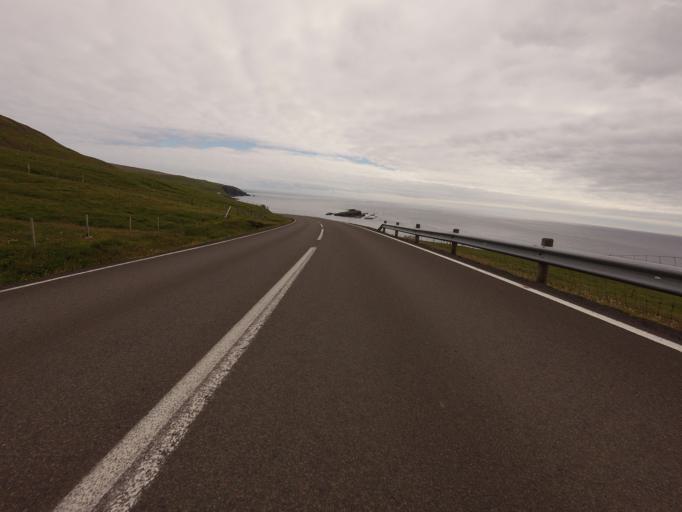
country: FO
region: Suduroy
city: Vagur
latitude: 61.4106
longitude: -6.7421
